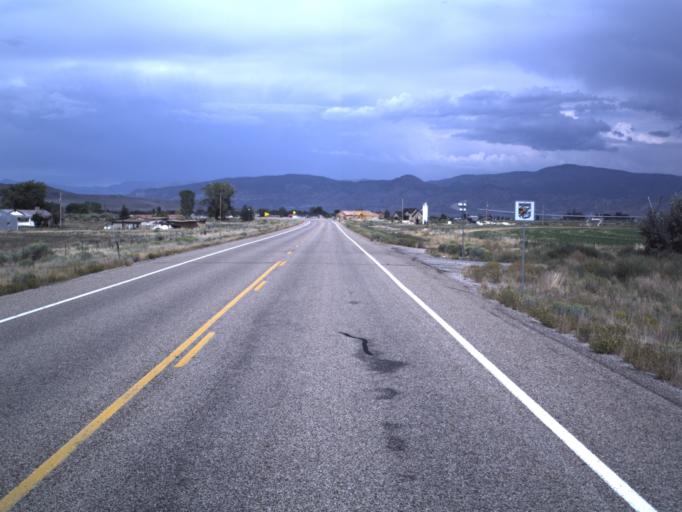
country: US
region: Utah
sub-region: Piute County
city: Junction
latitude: 38.1548
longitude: -112.2839
